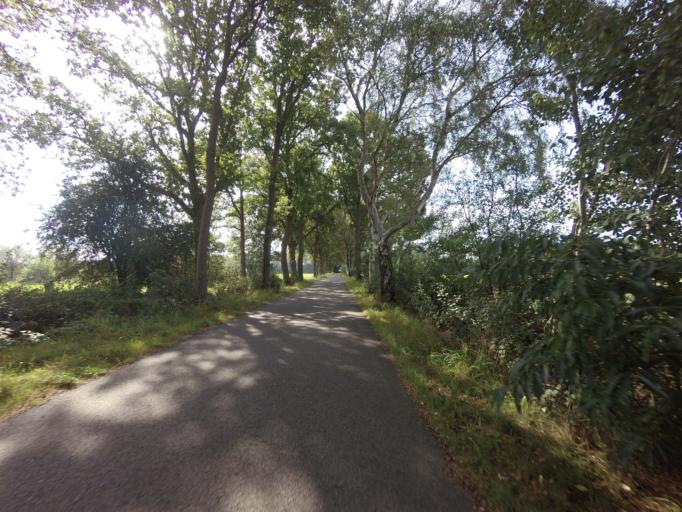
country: NL
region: Overijssel
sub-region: Gemeente Deventer
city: Schalkhaar
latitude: 52.2845
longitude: 6.2602
